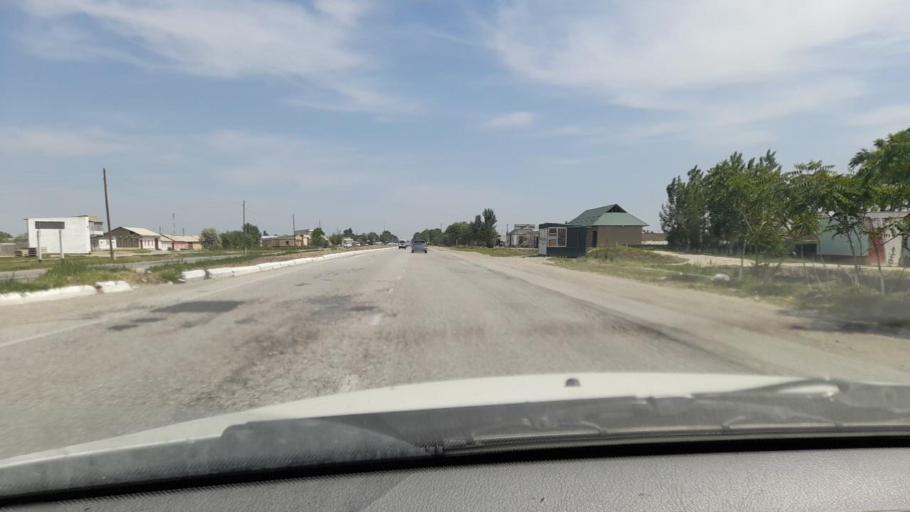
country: UZ
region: Navoiy
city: Navoiy
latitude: 40.1137
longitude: 65.5028
